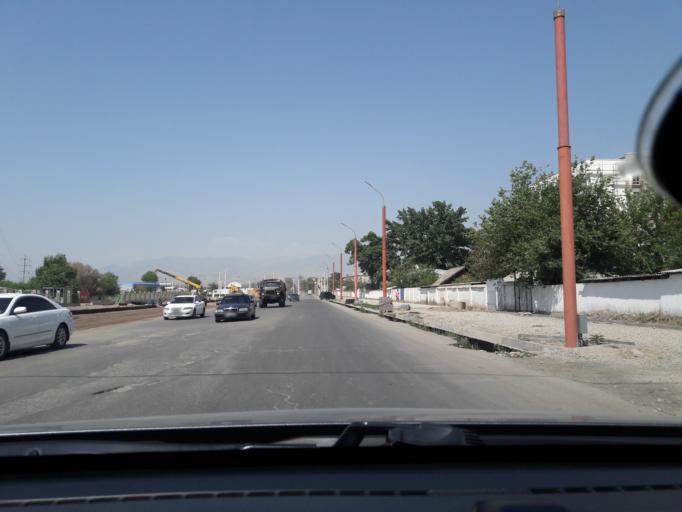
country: TJ
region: Dushanbe
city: Dushanbe
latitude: 38.5347
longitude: 68.7394
